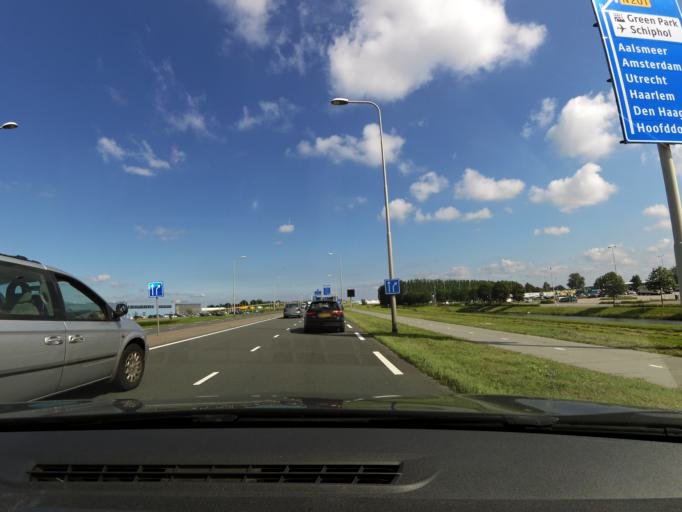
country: NL
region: North Holland
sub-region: Gemeente Aalsmeer
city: Aalsmeer
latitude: 52.2591
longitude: 4.7909
